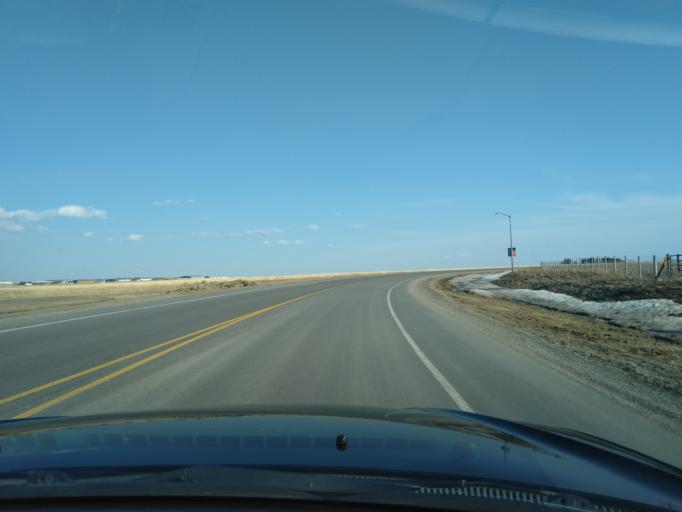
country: CA
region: Alberta
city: Cochrane
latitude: 51.1036
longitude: -114.3891
